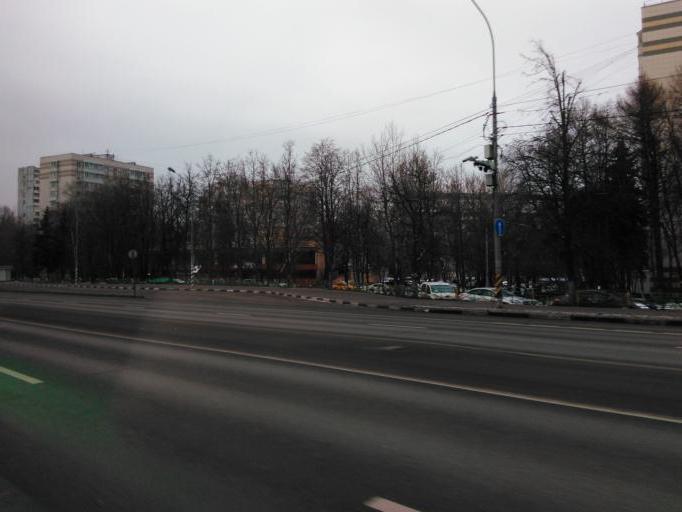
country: RU
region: Moscow
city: Zyuzino
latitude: 55.6503
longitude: 37.5583
